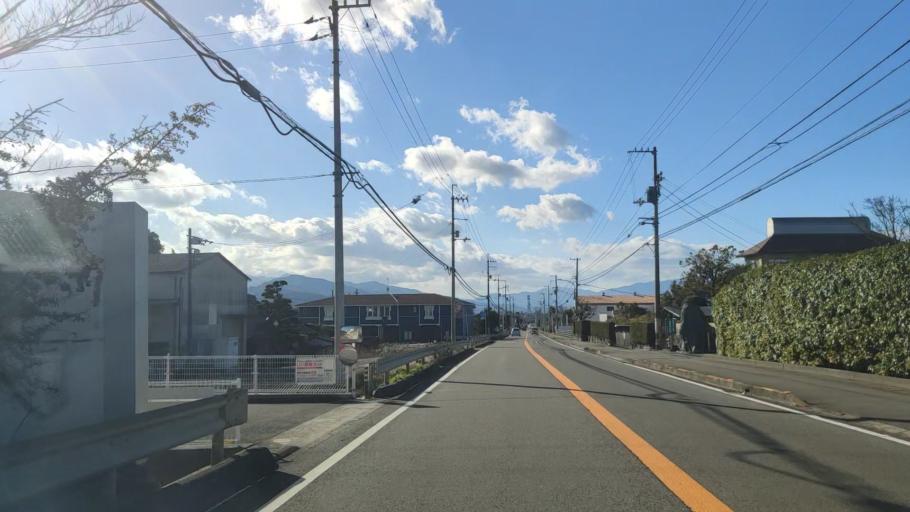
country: JP
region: Ehime
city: Saijo
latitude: 33.9154
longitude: 133.2161
